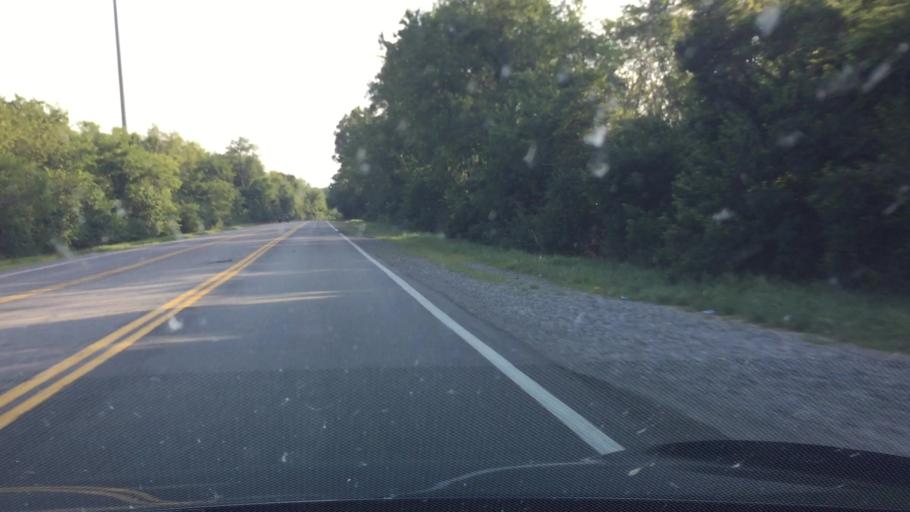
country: US
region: Virginia
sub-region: Pulaski County
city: Dublin
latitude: 37.1256
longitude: -80.6501
